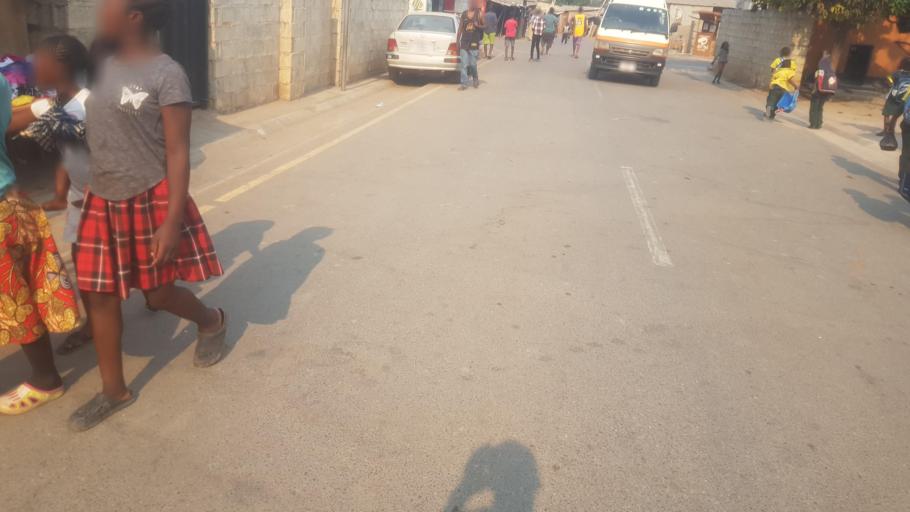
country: ZM
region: Lusaka
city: Lusaka
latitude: -15.4410
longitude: 28.3815
